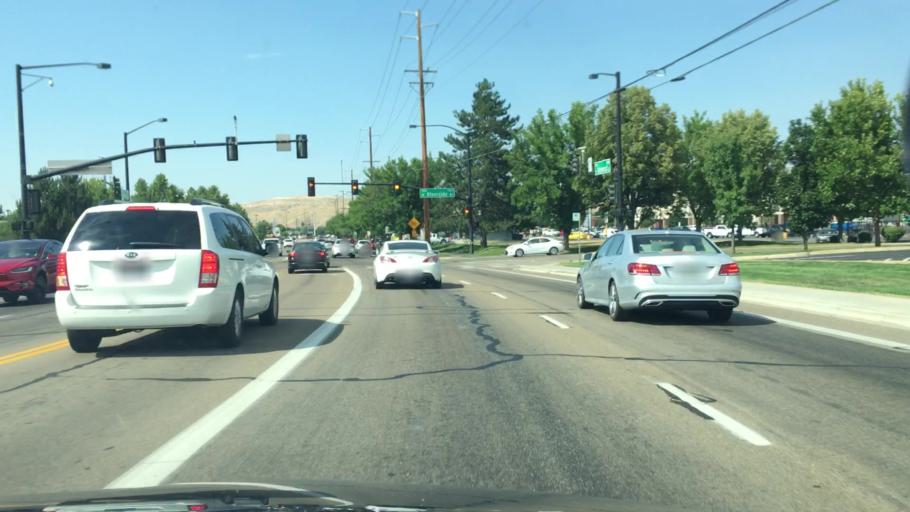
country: US
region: Idaho
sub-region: Ada County
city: Garden City
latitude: 43.6631
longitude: -116.2793
